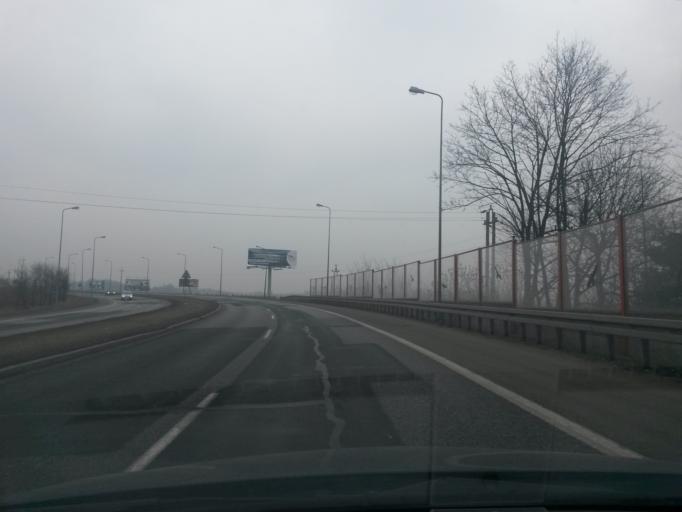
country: PL
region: Masovian Voivodeship
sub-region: Powiat legionowski
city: Bialobrzegi
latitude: 52.4663
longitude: 21.0291
